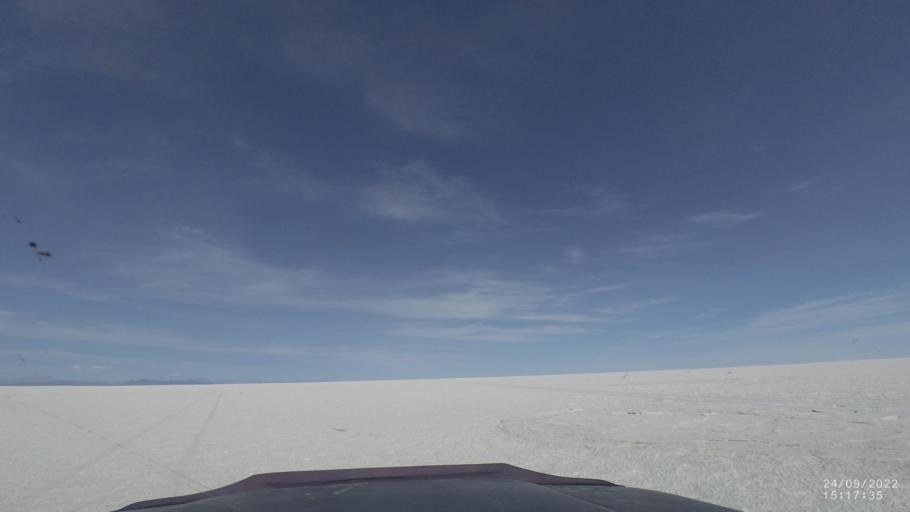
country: BO
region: Potosi
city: Colchani
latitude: -19.9904
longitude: -67.4258
